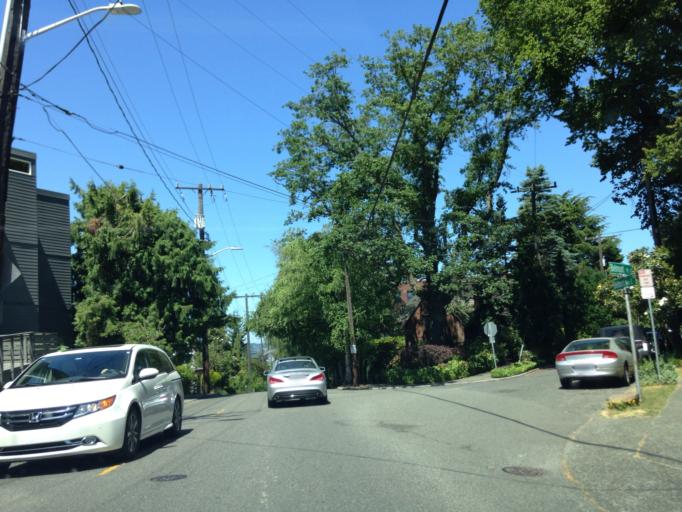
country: US
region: Washington
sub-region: King County
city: Seattle
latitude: 47.6253
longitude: -122.3242
